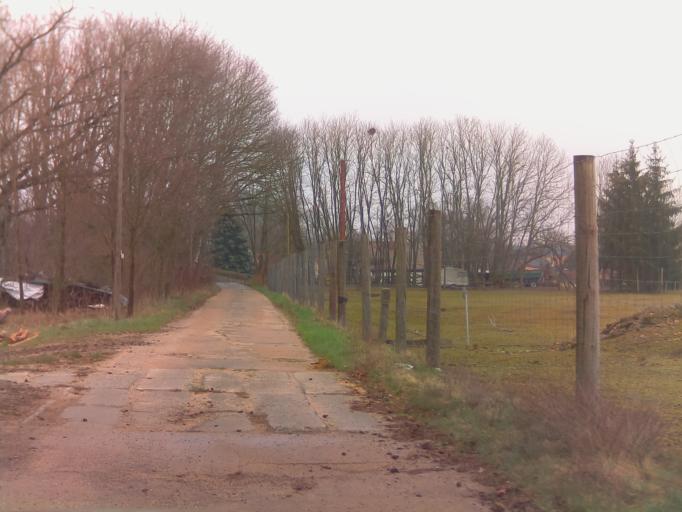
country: DE
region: Brandenburg
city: Neu Zauche
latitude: 51.9634
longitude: 14.1300
